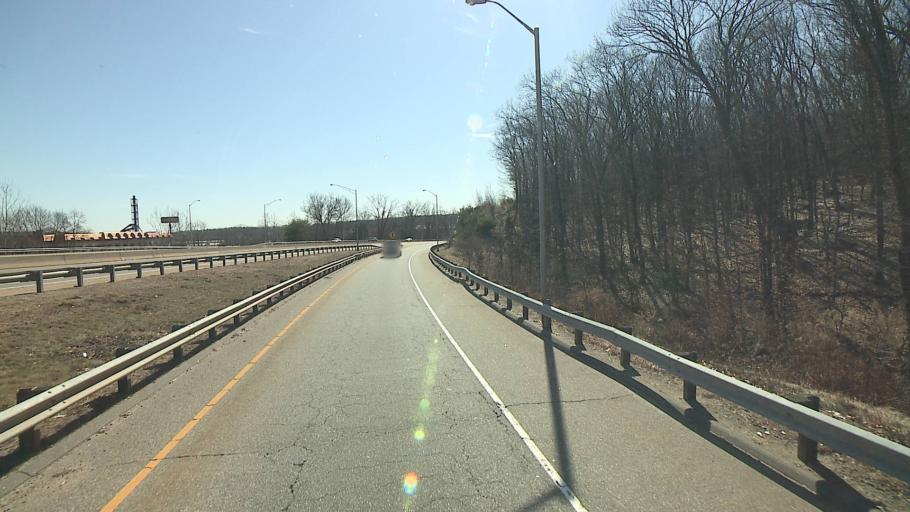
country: US
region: Connecticut
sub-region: New London County
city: Norwich
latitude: 41.5557
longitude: -72.1184
